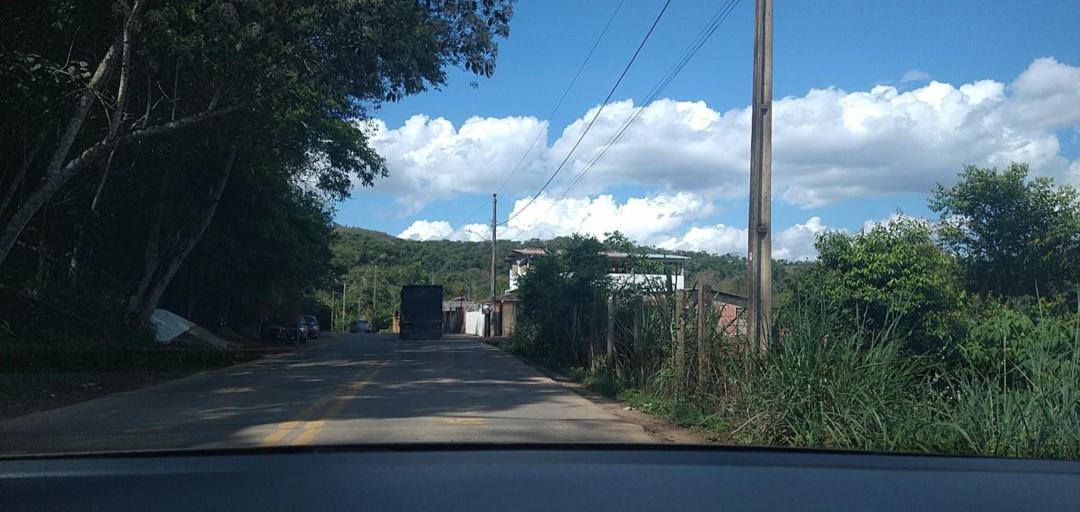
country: BR
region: Minas Gerais
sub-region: Rio Piracicaba
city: Rio Piracicaba
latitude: -19.9532
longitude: -43.1758
